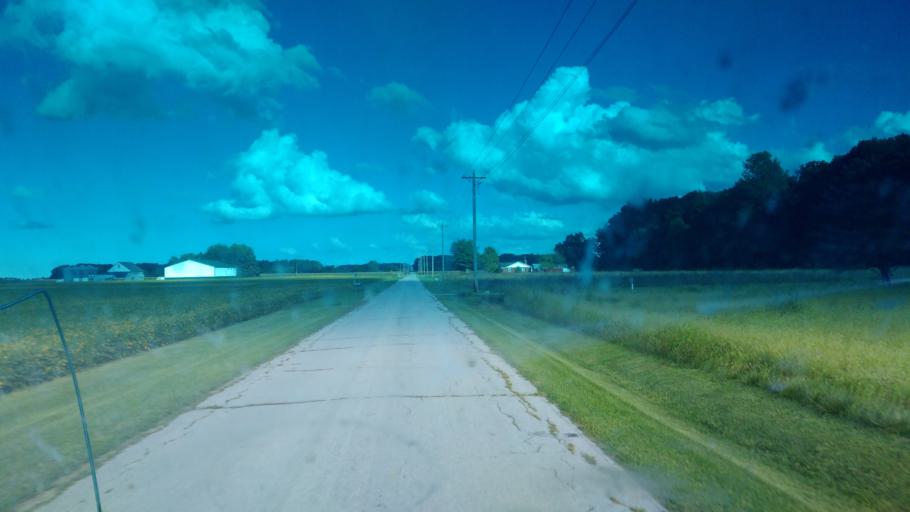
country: US
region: Ohio
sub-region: Hancock County
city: Arlington
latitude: 40.9364
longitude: -83.7519
